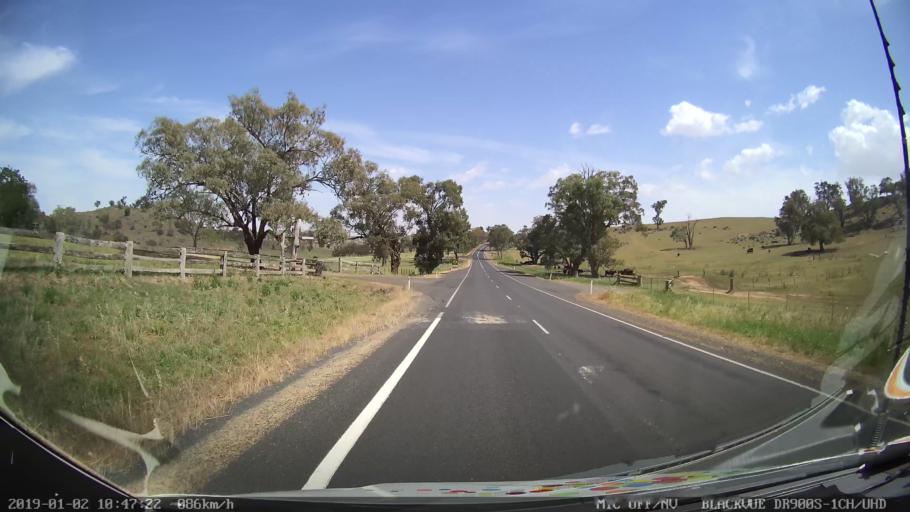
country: AU
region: New South Wales
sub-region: Cootamundra
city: Cootamundra
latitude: -34.7458
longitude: 148.2741
